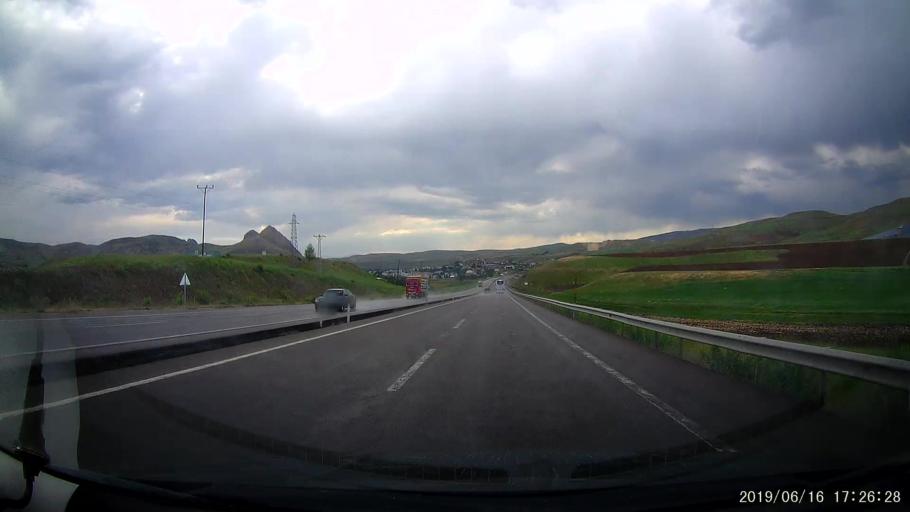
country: TR
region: Erzincan
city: Tercan
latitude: 39.7680
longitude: 40.4119
